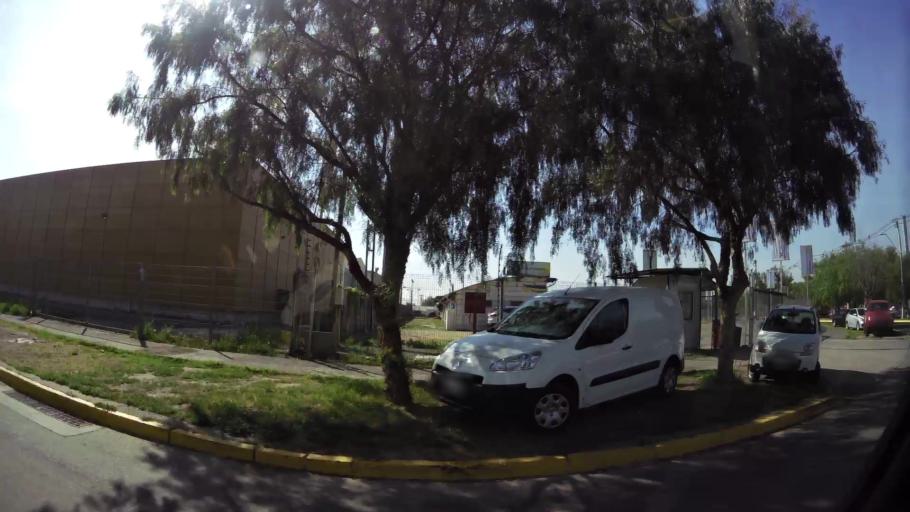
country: CL
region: Santiago Metropolitan
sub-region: Provincia de Santiago
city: Lo Prado
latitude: -33.4224
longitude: -70.7805
